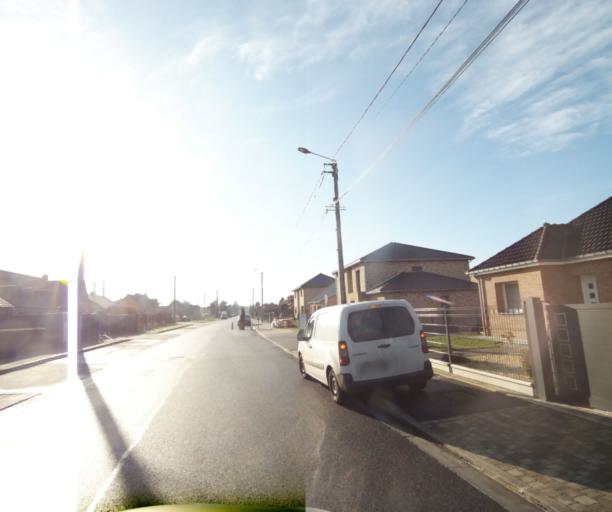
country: FR
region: Nord-Pas-de-Calais
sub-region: Departement du Nord
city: Trith-Saint-Leger
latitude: 50.3163
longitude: 3.4941
